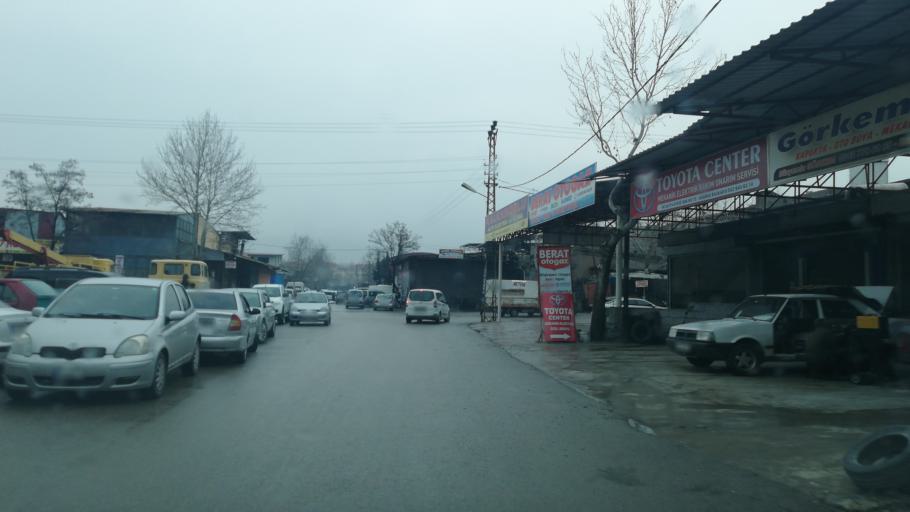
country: TR
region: Kahramanmaras
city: Kahramanmaras
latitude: 37.5649
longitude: 36.9594
